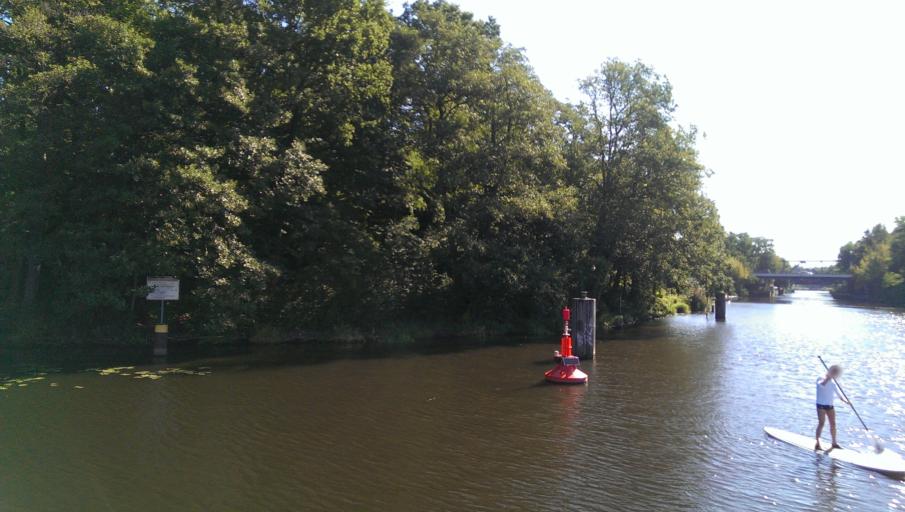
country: DE
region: Berlin
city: Wannsee
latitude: 52.4014
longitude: 13.1394
